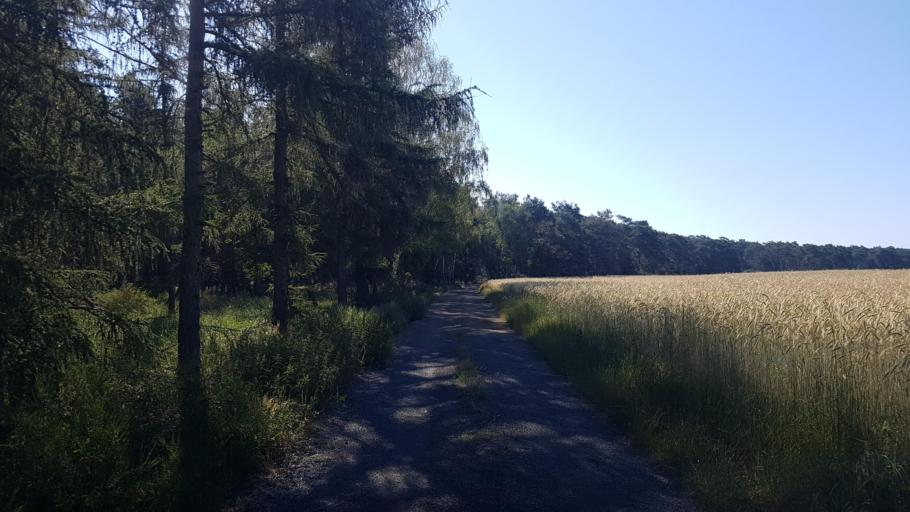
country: DE
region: Brandenburg
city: Juterbog
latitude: 51.9535
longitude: 13.1866
